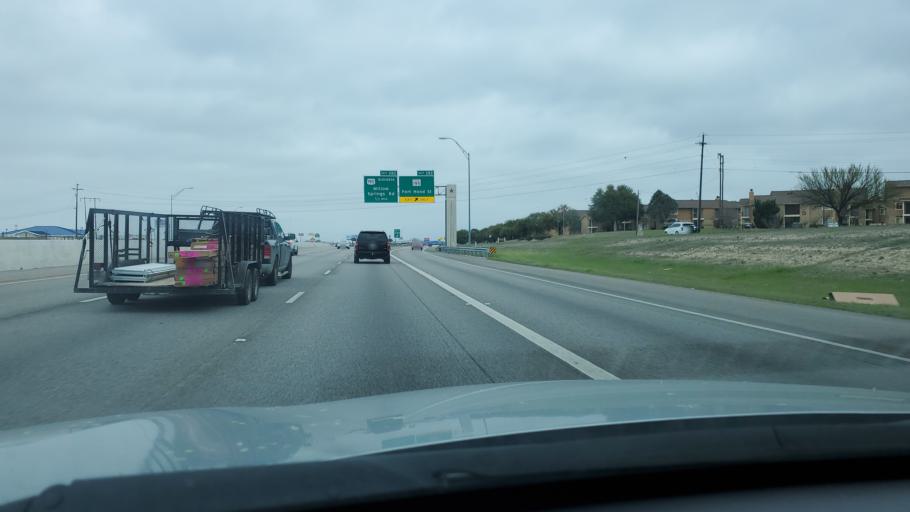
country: US
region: Texas
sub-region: Bell County
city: Killeen
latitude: 31.1032
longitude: -97.7419
